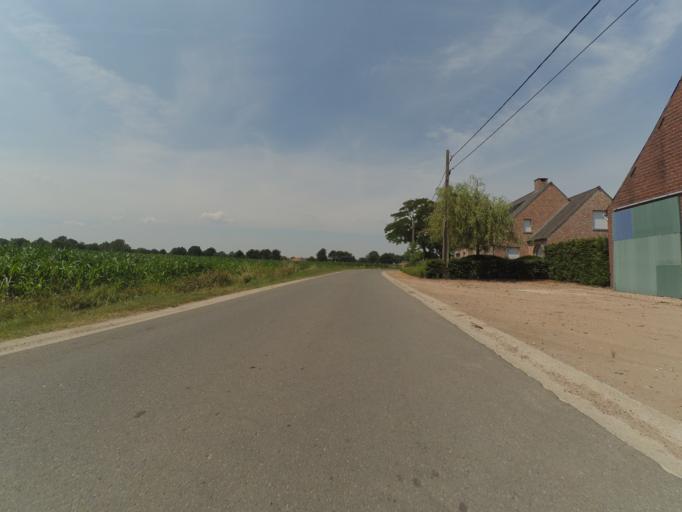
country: BE
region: Flanders
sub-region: Provincie Antwerpen
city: Wuustwezel
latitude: 51.4119
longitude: 4.5951
